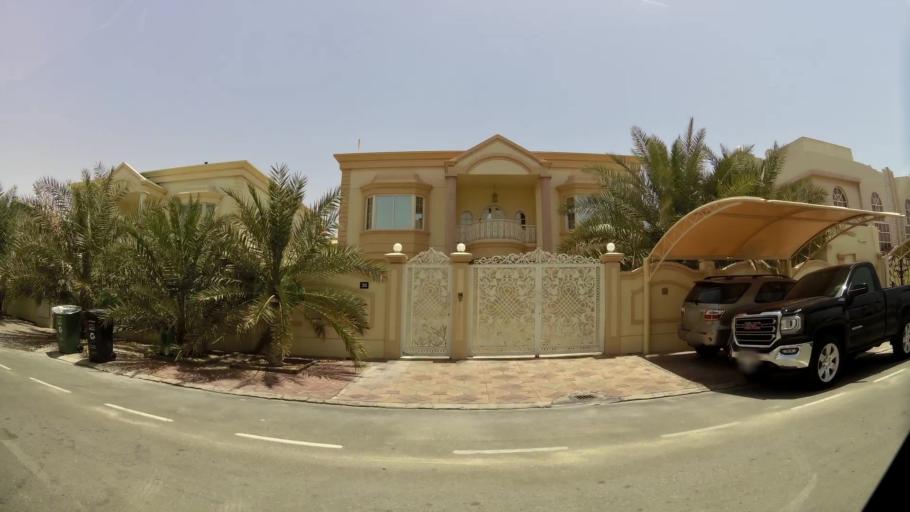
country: AE
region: Dubai
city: Dubai
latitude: 25.1734
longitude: 55.2203
